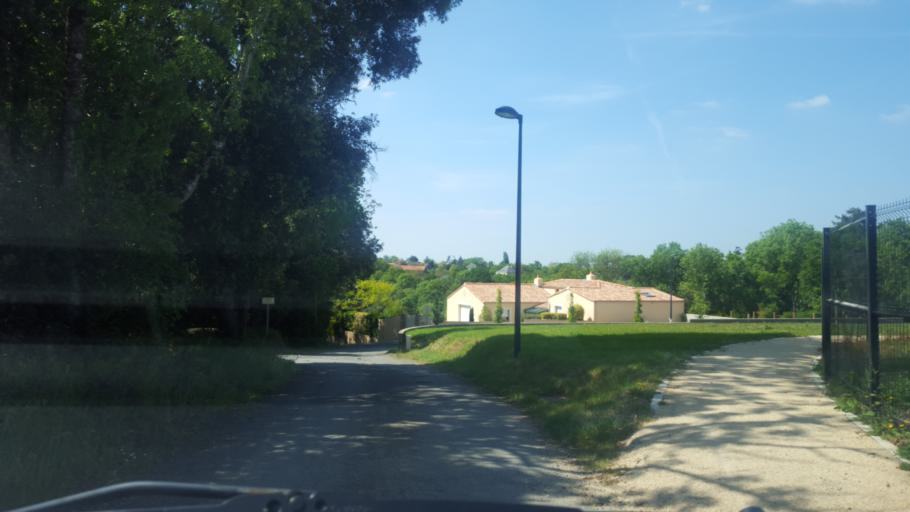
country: FR
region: Pays de la Loire
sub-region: Departement de la Loire-Atlantique
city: La Limouziniere
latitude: 46.9618
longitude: -1.5774
